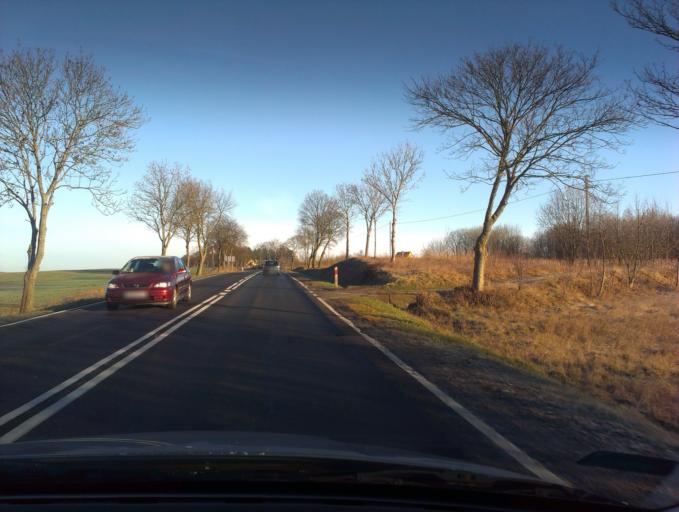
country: PL
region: West Pomeranian Voivodeship
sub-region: Powiat szczecinecki
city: Szczecinek
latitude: 53.7366
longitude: 16.6682
